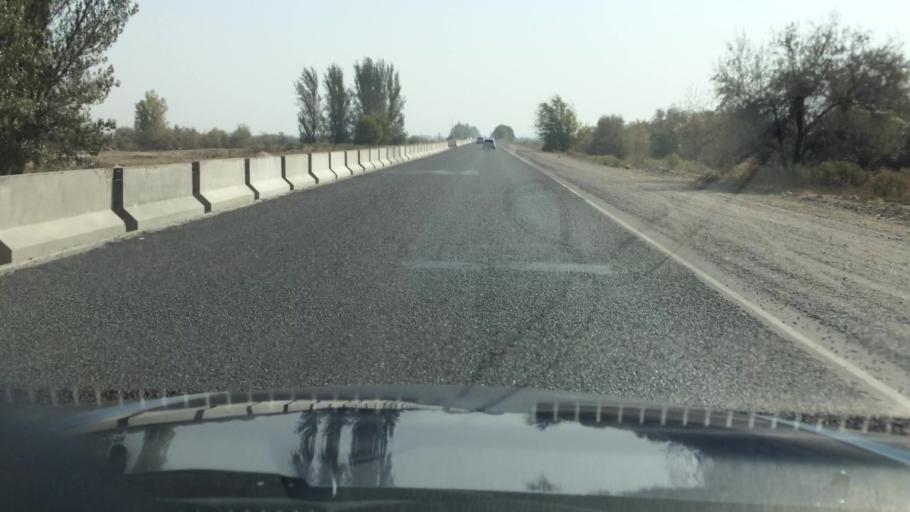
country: KG
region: Chuy
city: Kant
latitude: 42.9728
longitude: 74.8983
